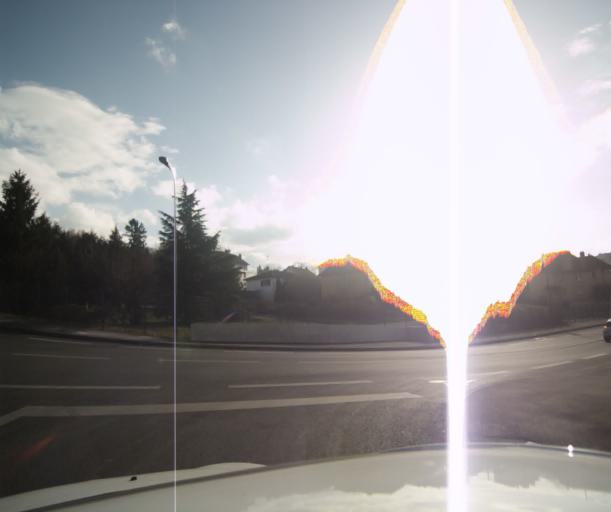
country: FR
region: Franche-Comte
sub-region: Departement du Doubs
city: Besancon
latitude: 47.2478
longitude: 6.0384
